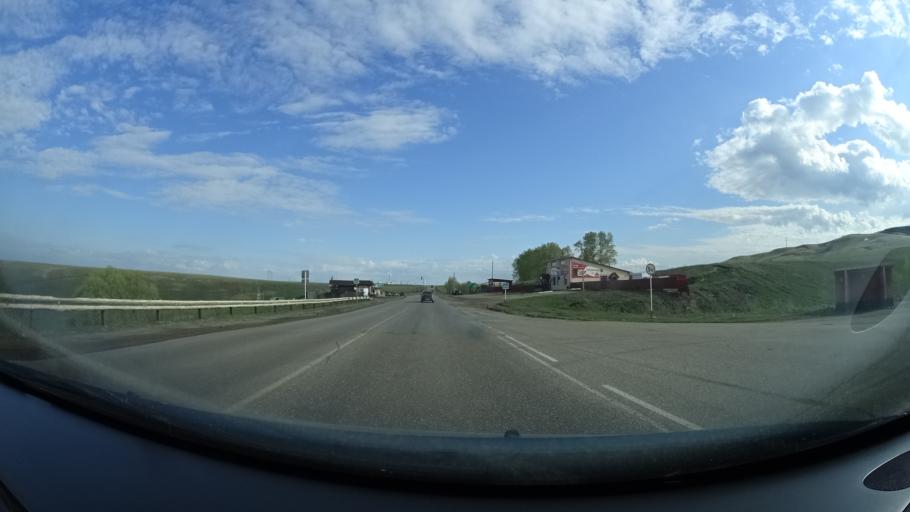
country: RU
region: Bashkortostan
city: Blagoveshchensk
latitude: 55.1718
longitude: 55.8536
